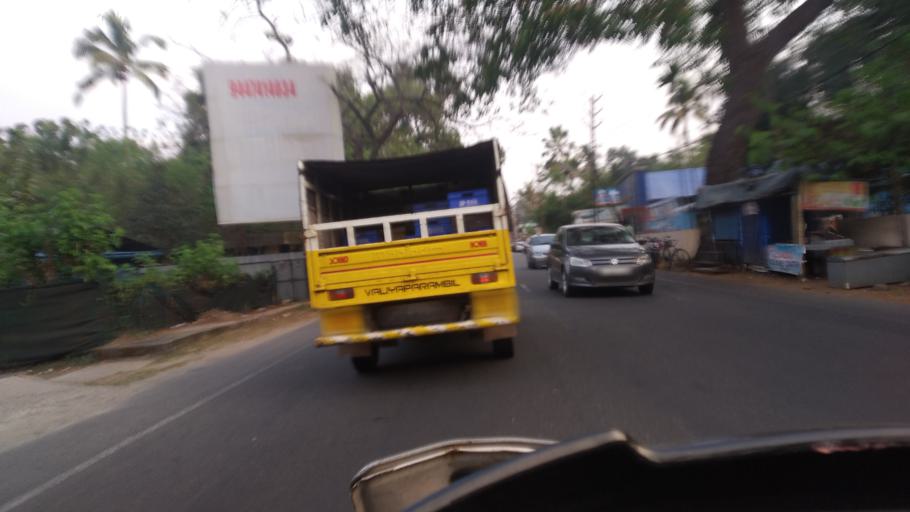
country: IN
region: Kerala
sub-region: Thrissur District
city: Kodungallur
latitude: 10.2415
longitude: 76.1918
